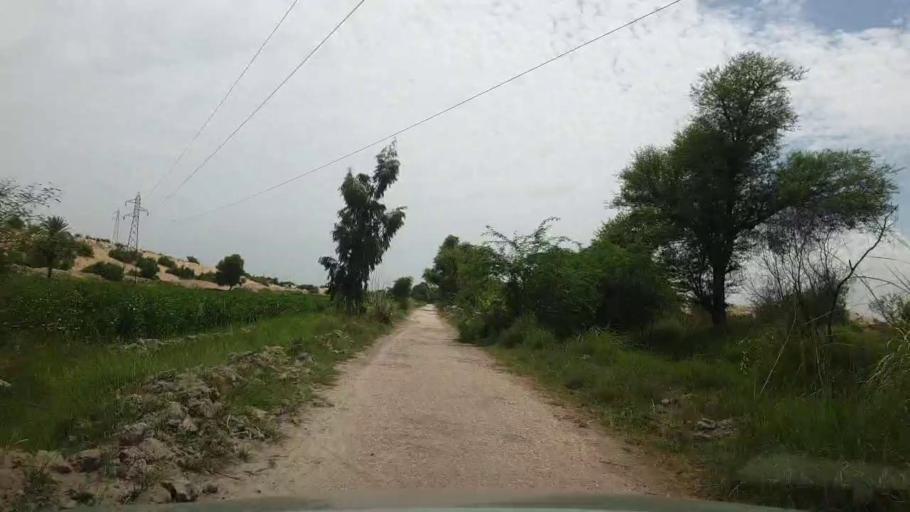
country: PK
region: Sindh
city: Bozdar
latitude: 27.0679
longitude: 68.9670
